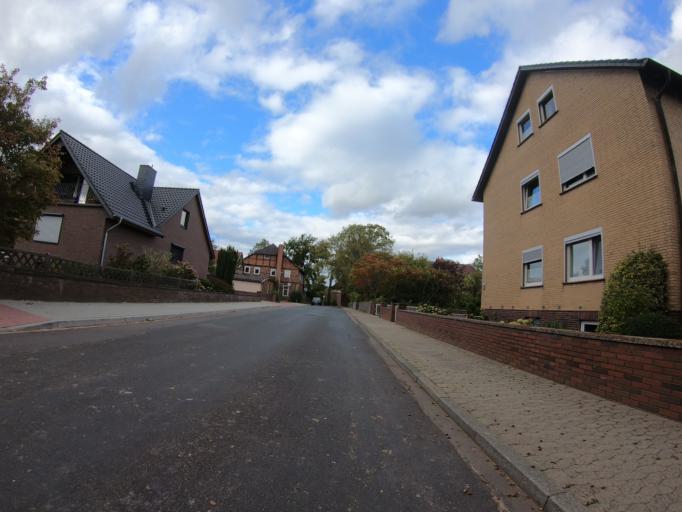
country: DE
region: Lower Saxony
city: Wasbuttel
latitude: 52.4105
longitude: 10.5927
